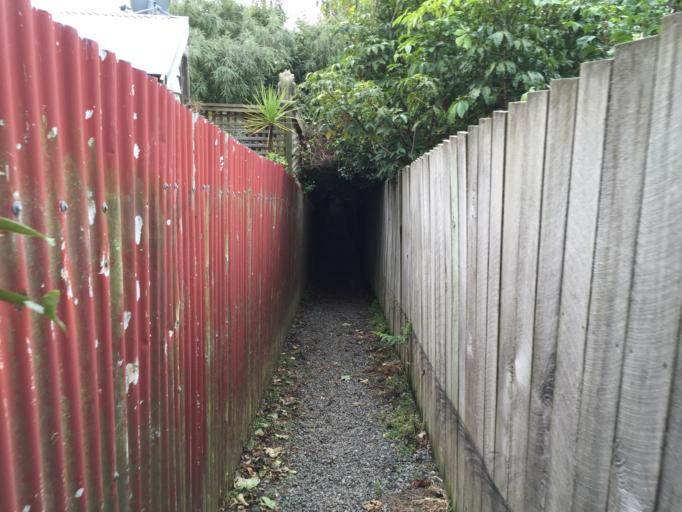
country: NZ
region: Southland
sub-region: Southland District
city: Riverton
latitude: -46.3722
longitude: 168.0272
